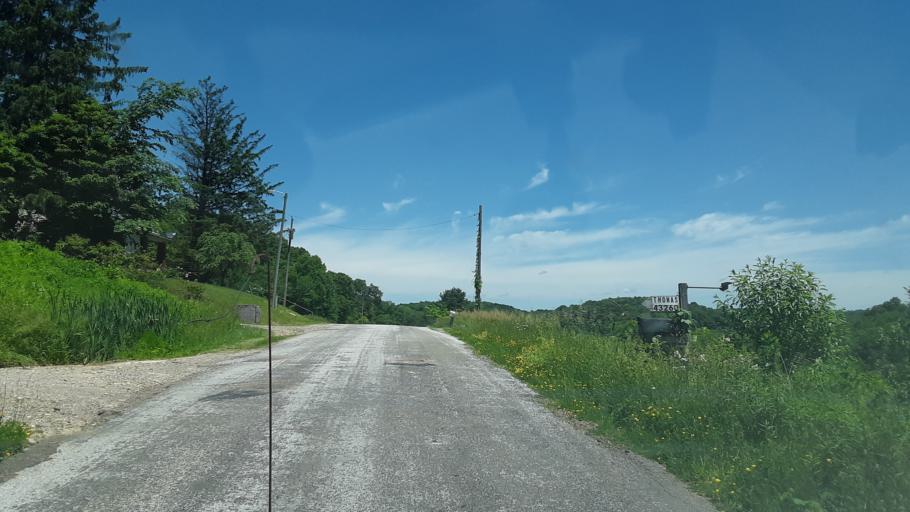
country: US
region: Ohio
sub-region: Coshocton County
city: Coshocton
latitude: 40.2691
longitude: -81.9506
